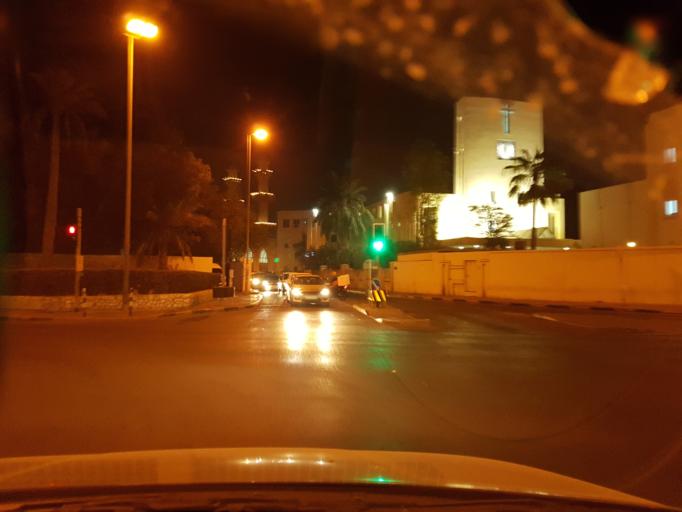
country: BH
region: Manama
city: Manama
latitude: 26.2323
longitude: 50.5821
